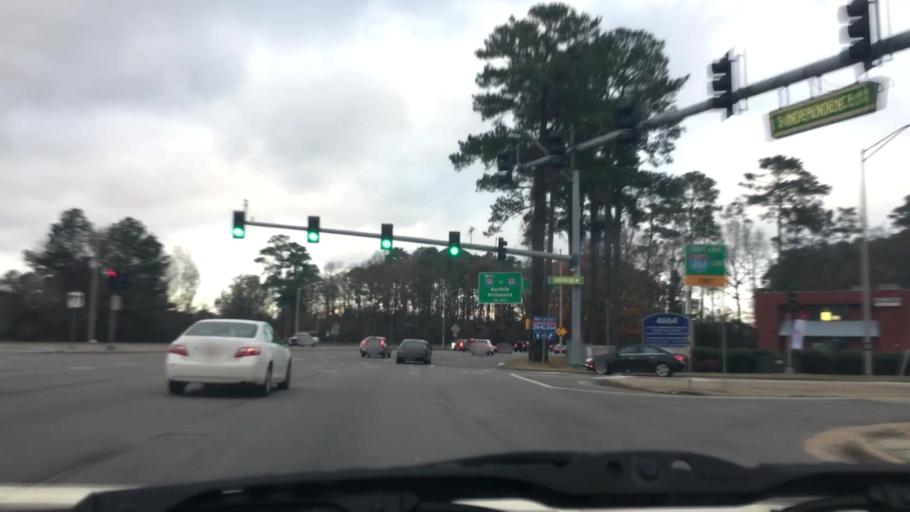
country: US
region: Virginia
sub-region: City of Chesapeake
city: Chesapeake
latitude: 36.8307
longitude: -76.1371
